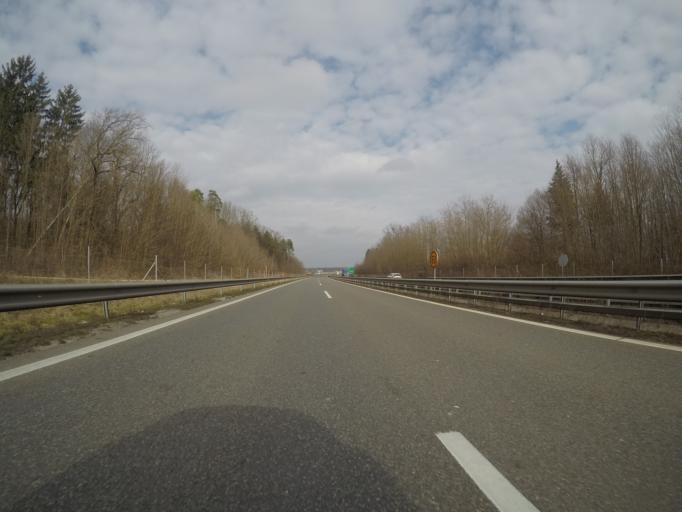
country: SI
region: Krizevci
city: Krizevci pri Ljutomeru
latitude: 46.5850
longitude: 16.0917
